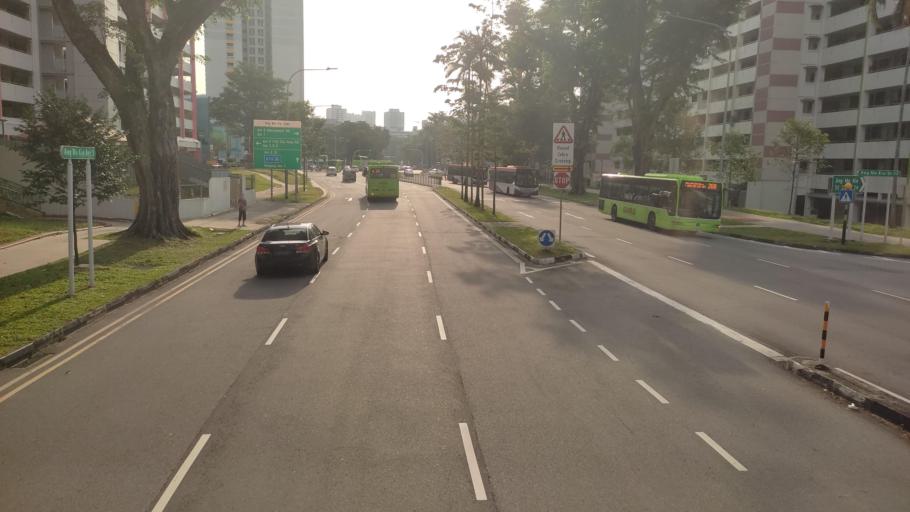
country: SG
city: Singapore
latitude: 1.3693
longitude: 103.8438
